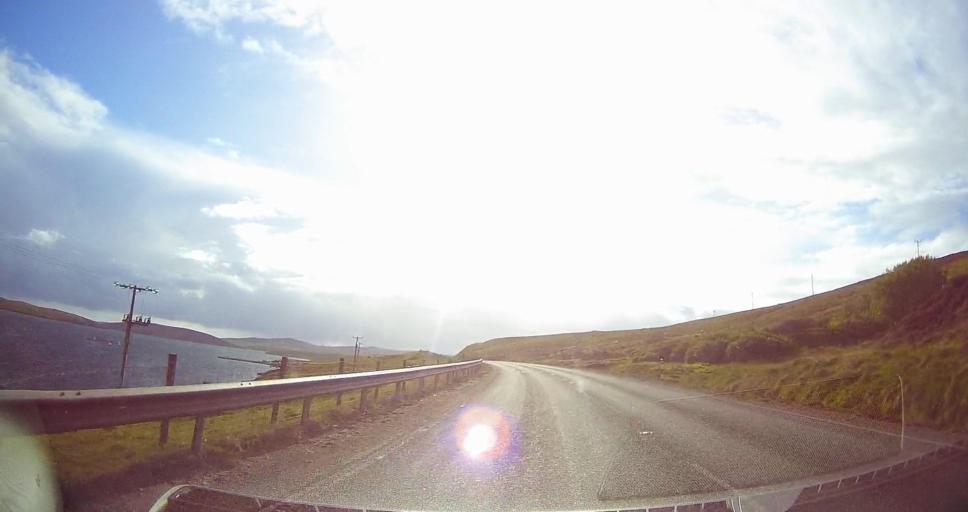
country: GB
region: Scotland
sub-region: Shetland Islands
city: Lerwick
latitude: 60.3701
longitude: -1.3026
